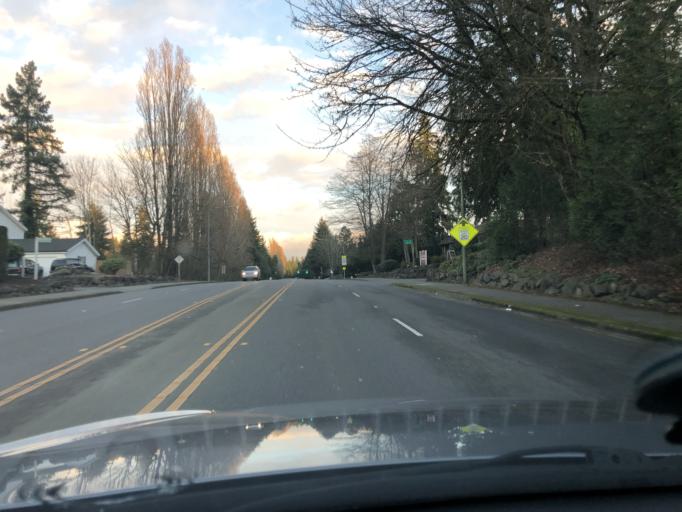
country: US
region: Washington
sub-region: Pierce County
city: Fife Heights
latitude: 47.3152
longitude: -122.3910
